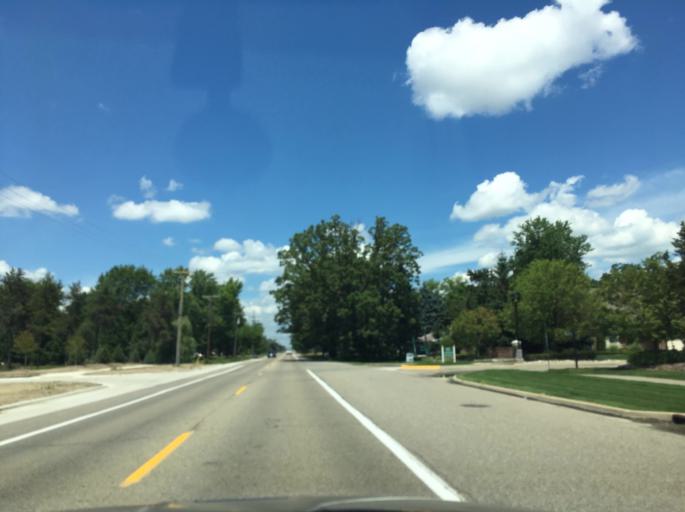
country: US
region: Michigan
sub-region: Macomb County
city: Mount Clemens
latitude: 42.6357
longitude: -82.8963
